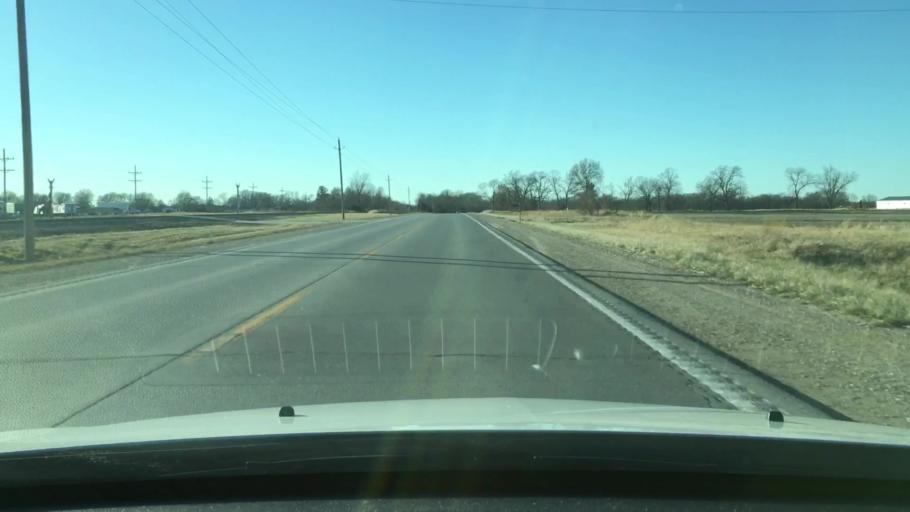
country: US
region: Missouri
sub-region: Audrain County
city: Mexico
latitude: 39.1884
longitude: -91.9719
